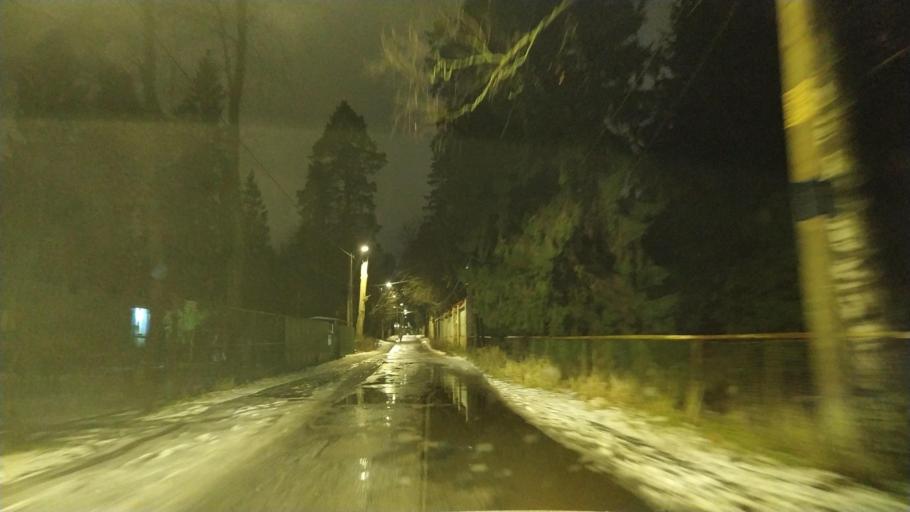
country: RU
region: Leningrad
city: Vsevolozhsk
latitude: 60.0237
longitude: 30.6792
